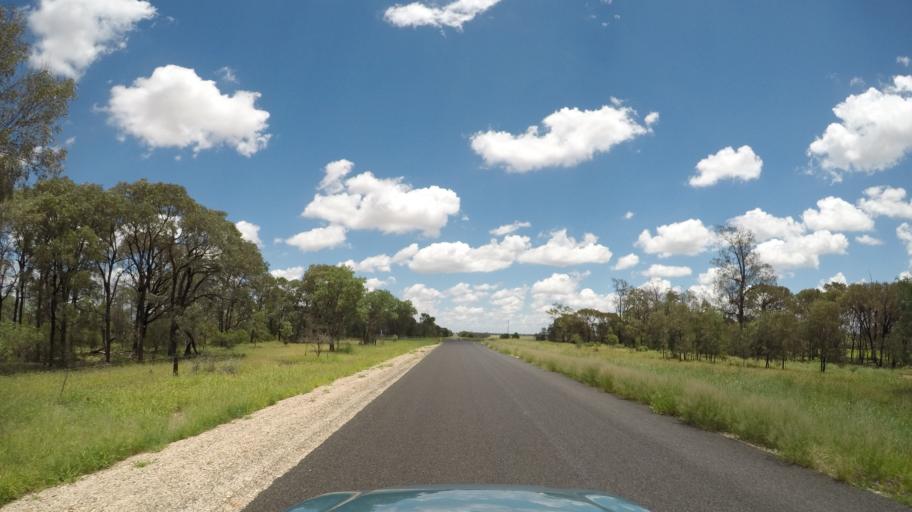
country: AU
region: Queensland
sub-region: Goondiwindi
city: Goondiwindi
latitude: -28.1668
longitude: 150.1835
